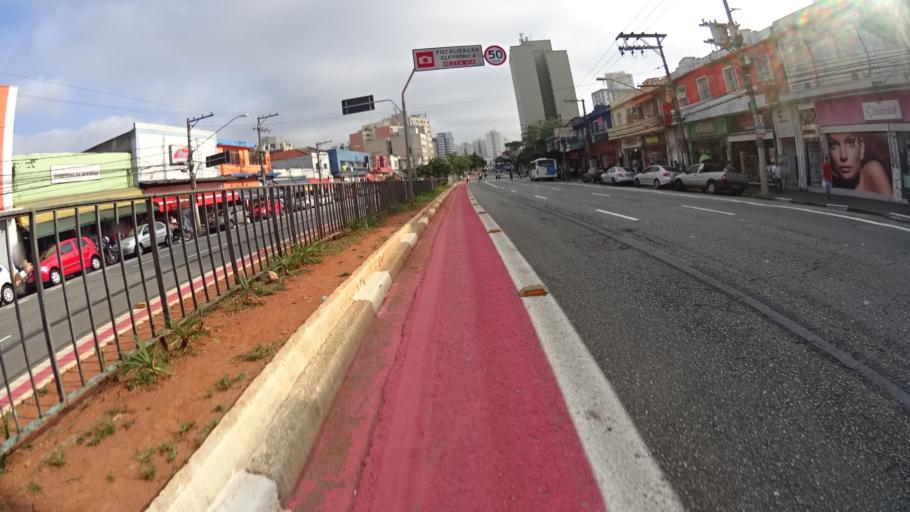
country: BR
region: Sao Paulo
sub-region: Sao Paulo
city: Sao Paulo
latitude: -23.6112
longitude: -46.6379
